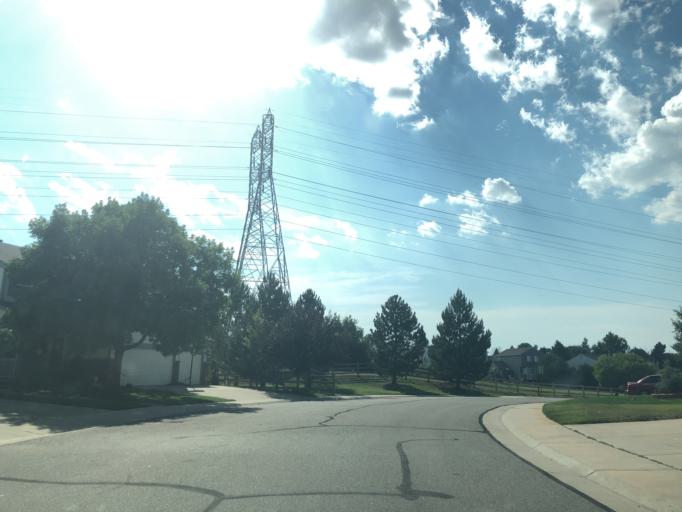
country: US
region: Colorado
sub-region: Arapahoe County
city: Dove Valley
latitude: 39.6367
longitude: -104.7531
